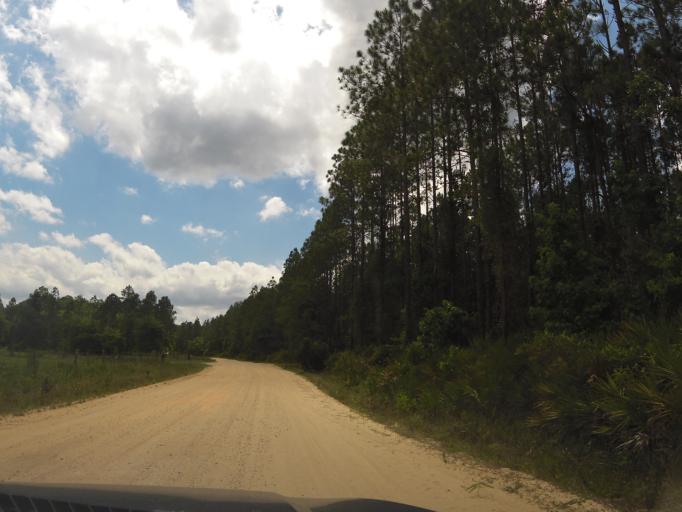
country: US
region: Florida
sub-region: Clay County
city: Asbury Lake
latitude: 29.9016
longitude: -81.8260
